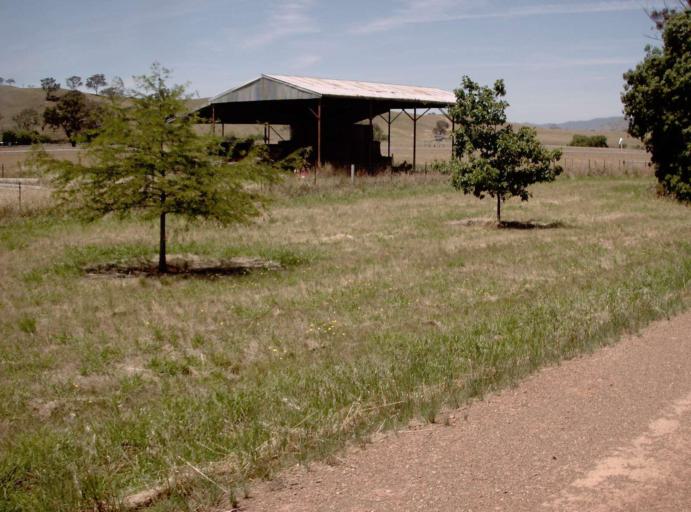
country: AU
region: Victoria
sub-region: East Gippsland
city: Bairnsdale
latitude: -37.2431
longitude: 147.7131
